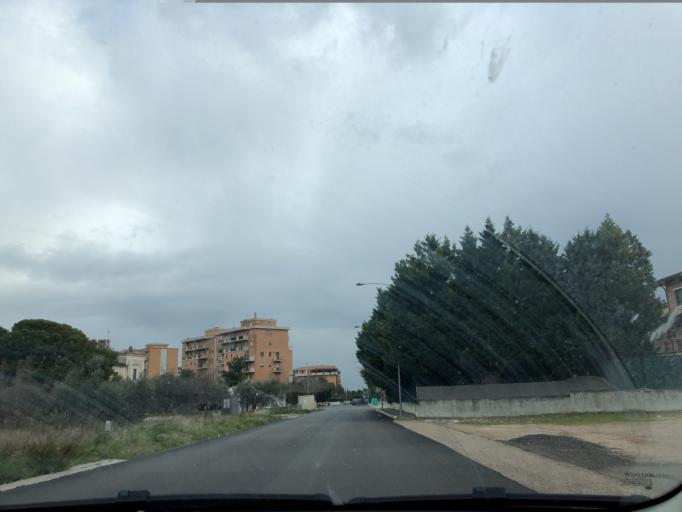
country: IT
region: Apulia
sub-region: Provincia di Foggia
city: Lucera
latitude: 41.5004
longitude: 15.3506
